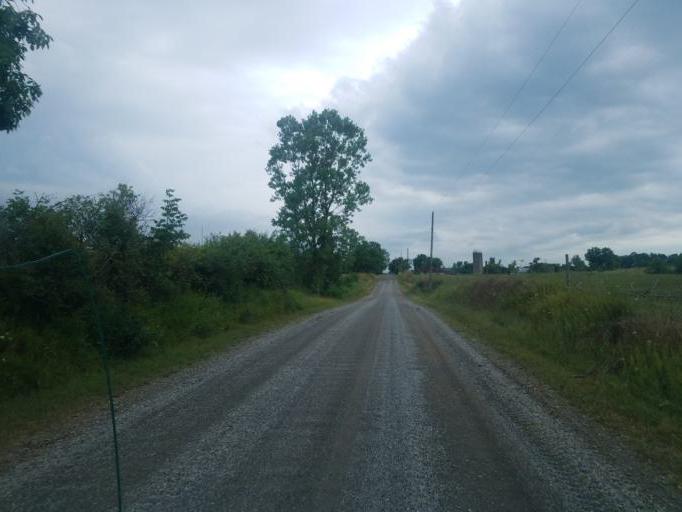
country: US
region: Ohio
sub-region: Defiance County
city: Hicksville
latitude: 41.3125
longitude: -84.8039
